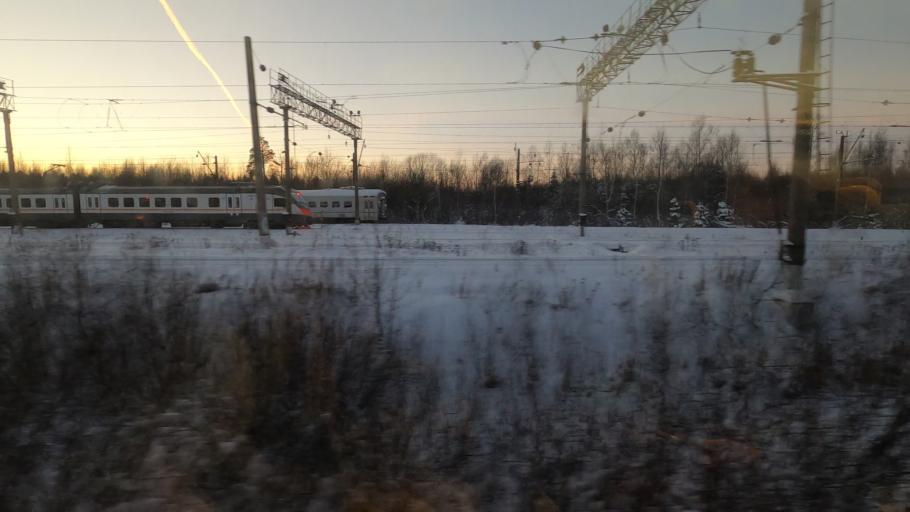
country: RU
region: Moskovskaya
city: Lugovaya
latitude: 56.0307
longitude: 37.4876
